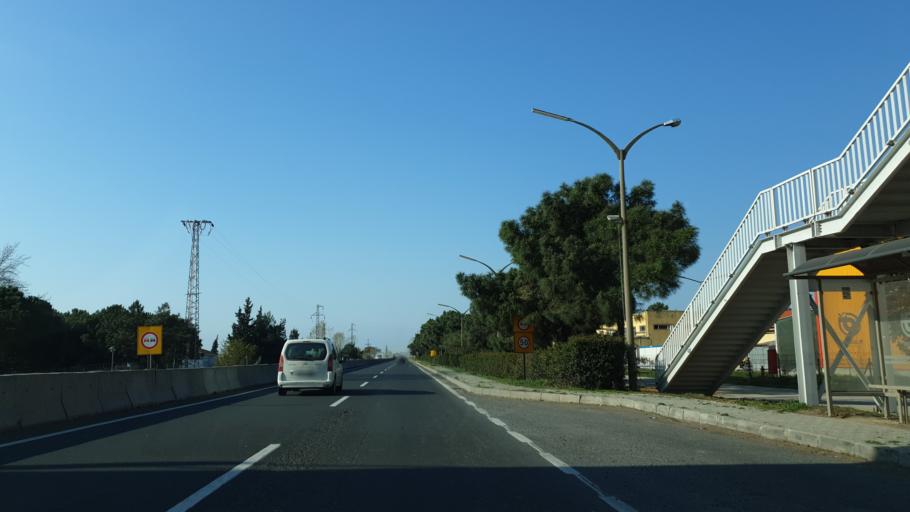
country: TR
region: Tekirdag
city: Corlu
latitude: 41.0199
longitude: 27.7216
